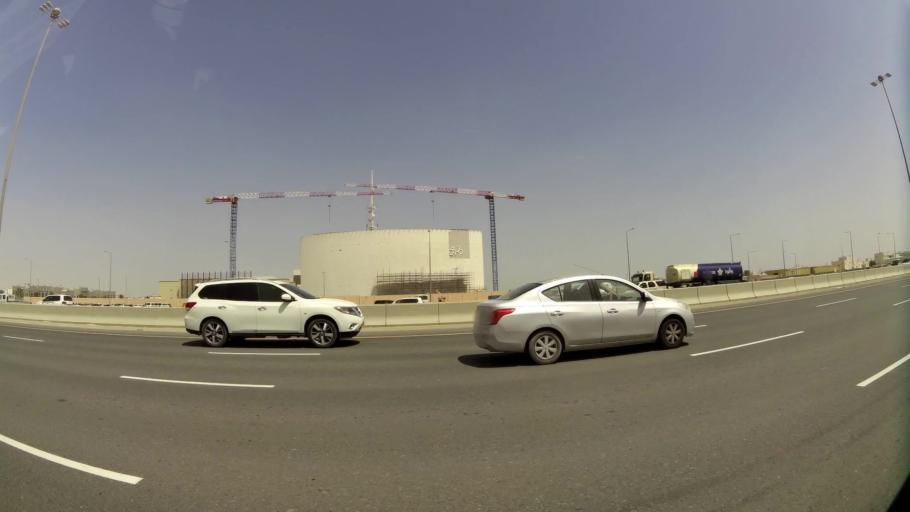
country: QA
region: Baladiyat ar Rayyan
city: Ar Rayyan
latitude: 25.3522
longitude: 51.4539
